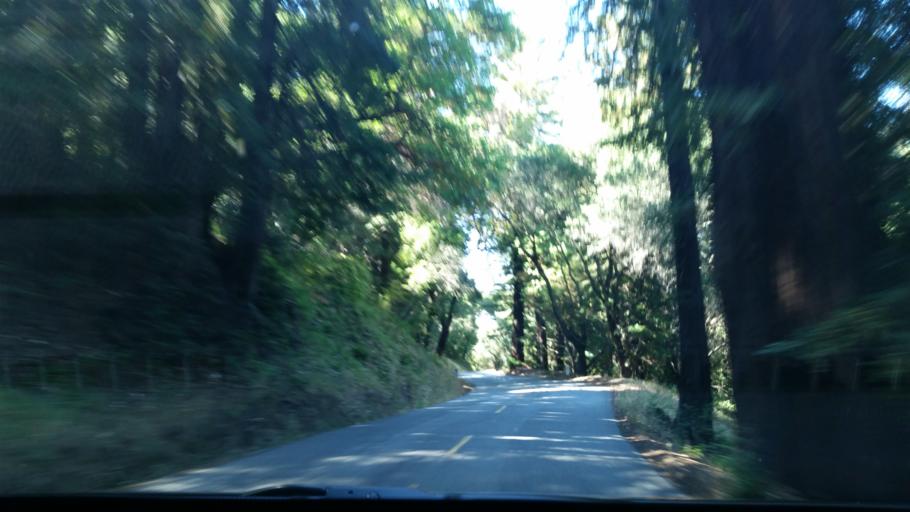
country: US
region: California
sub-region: San Mateo County
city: Emerald Lake Hills
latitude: 37.4355
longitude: -122.2930
